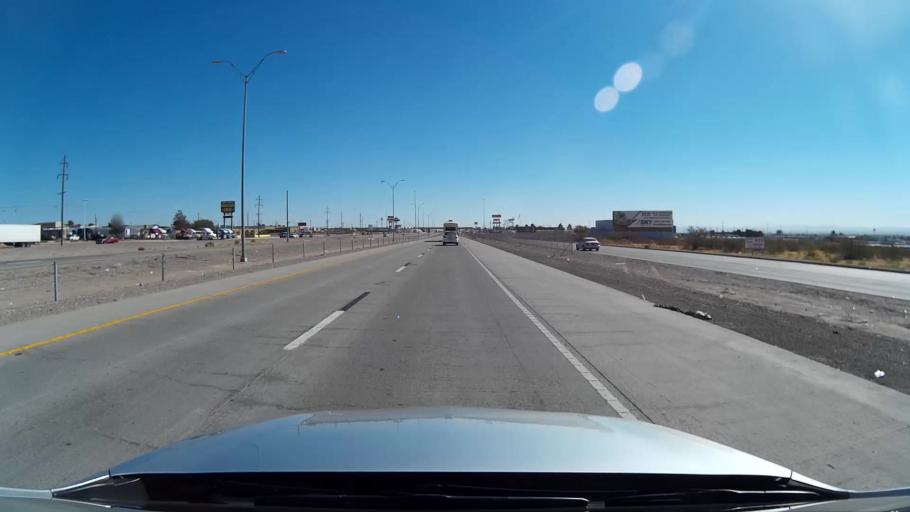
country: US
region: Texas
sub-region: El Paso County
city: Sparks
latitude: 31.6658
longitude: -106.2448
